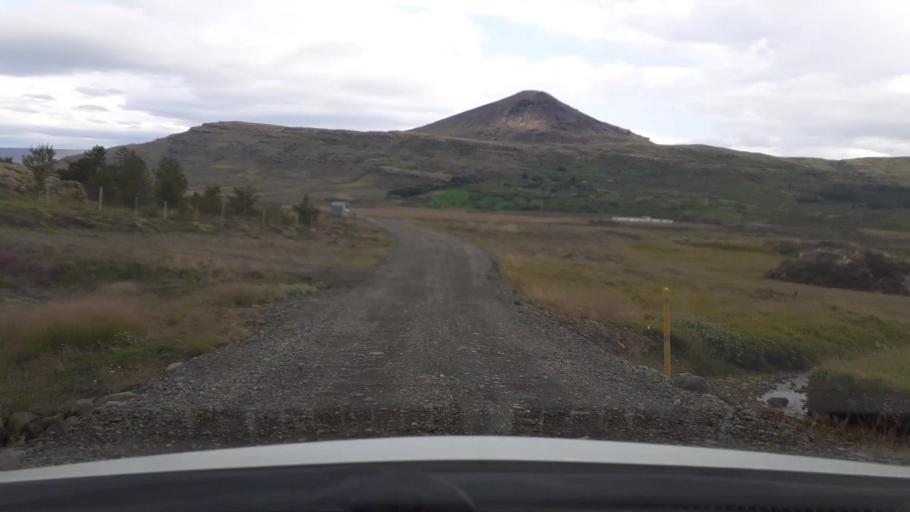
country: IS
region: Capital Region
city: Mosfellsbaer
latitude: 64.2896
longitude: -21.4606
